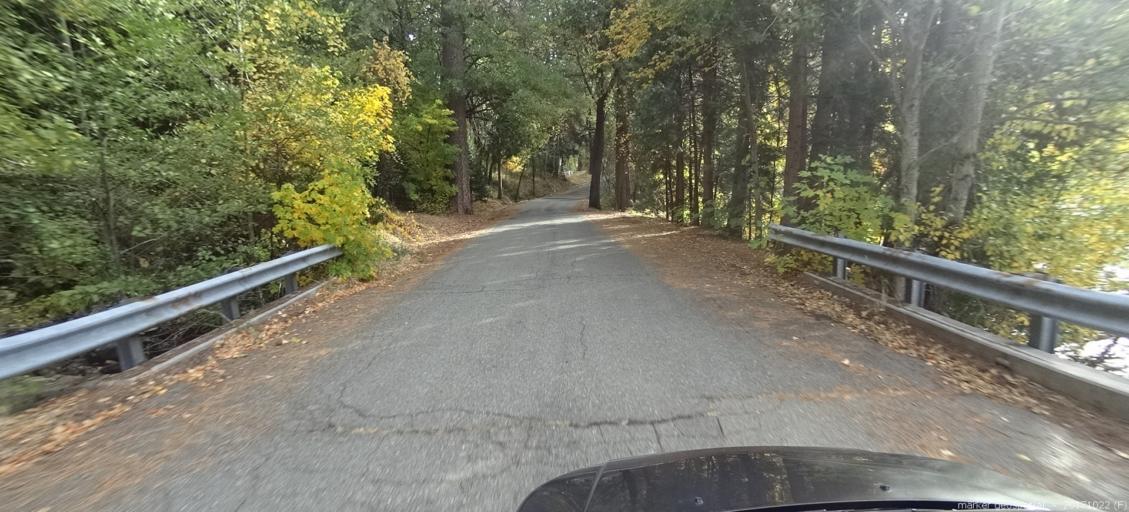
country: US
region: California
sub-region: Siskiyou County
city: Dunsmuir
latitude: 41.1474
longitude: -122.3235
